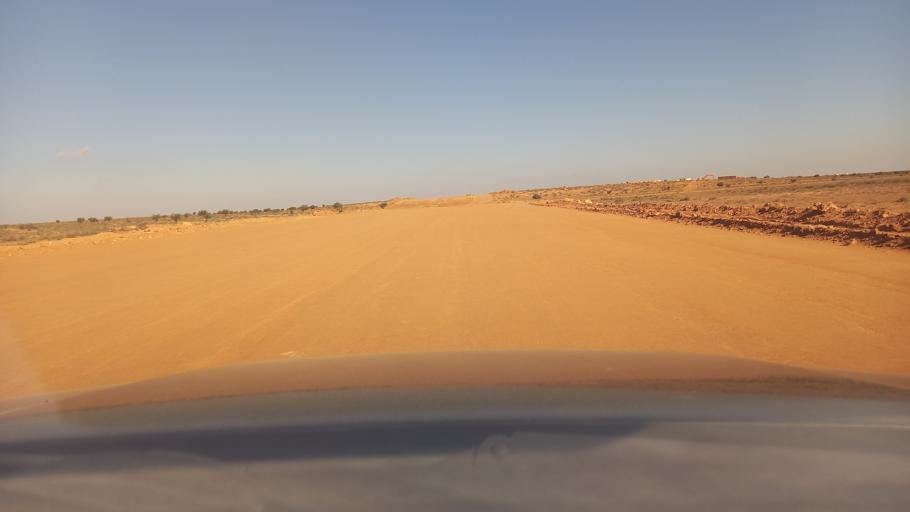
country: TN
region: Madanin
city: Medenine
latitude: 33.1712
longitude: 10.5264
